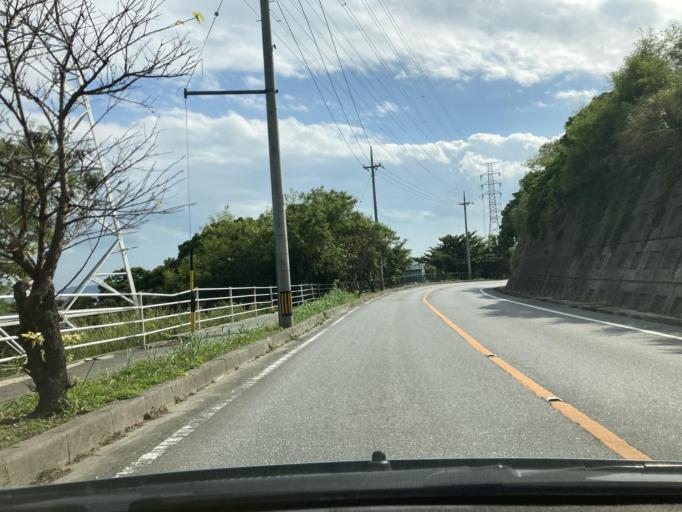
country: JP
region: Okinawa
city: Ginowan
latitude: 26.2593
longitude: 127.7852
